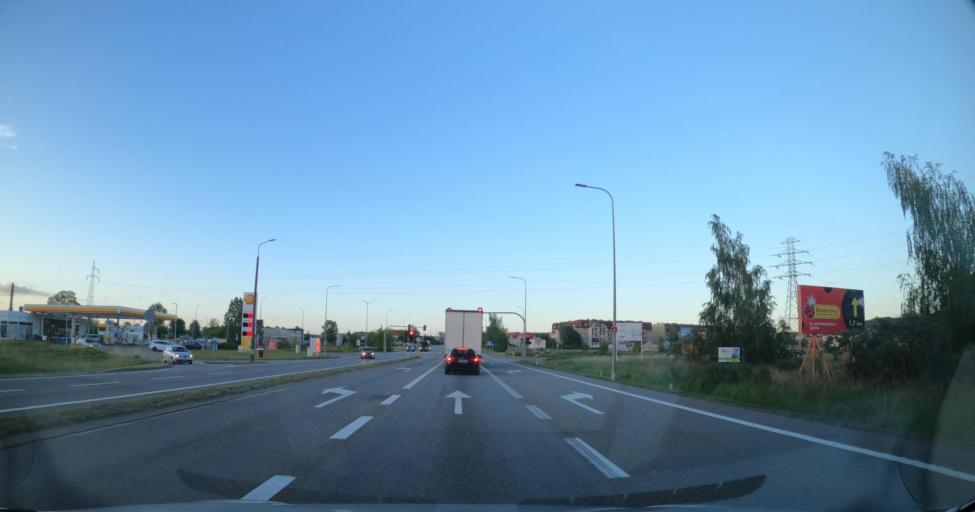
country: PL
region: Pomeranian Voivodeship
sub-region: Powiat leborski
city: Lebork
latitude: 54.5251
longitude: 17.7372
